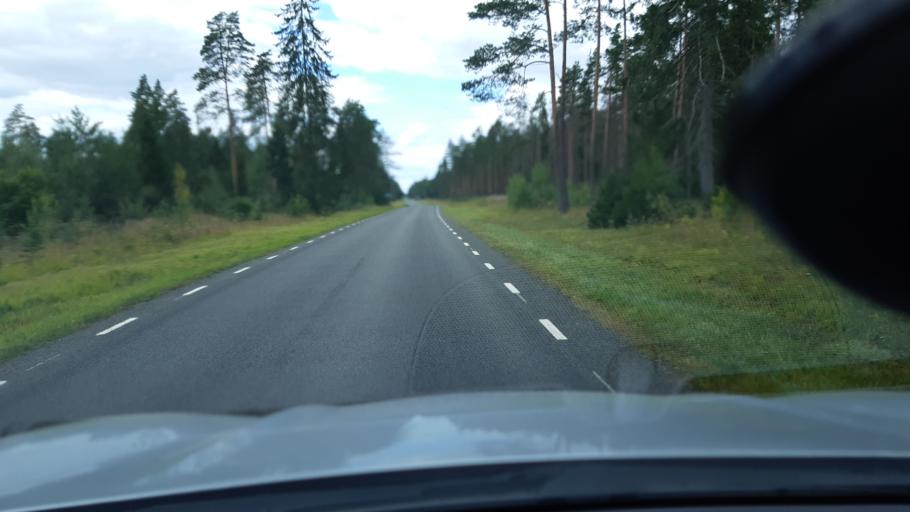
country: EE
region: Raplamaa
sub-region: Rapla vald
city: Rapla
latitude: 58.8946
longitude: 24.7055
